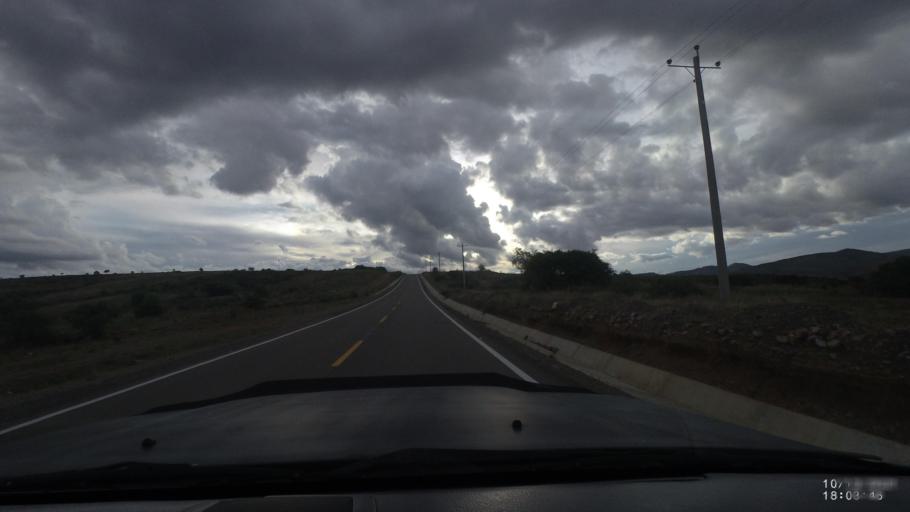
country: BO
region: Cochabamba
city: Cliza
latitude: -17.7625
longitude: -65.9209
